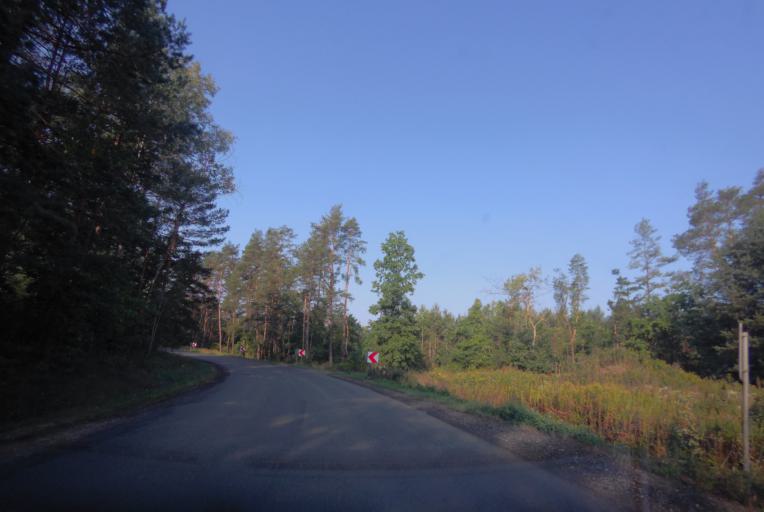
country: PL
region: Subcarpathian Voivodeship
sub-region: Powiat nizanski
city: Harasiuki
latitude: 50.5139
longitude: 22.4017
